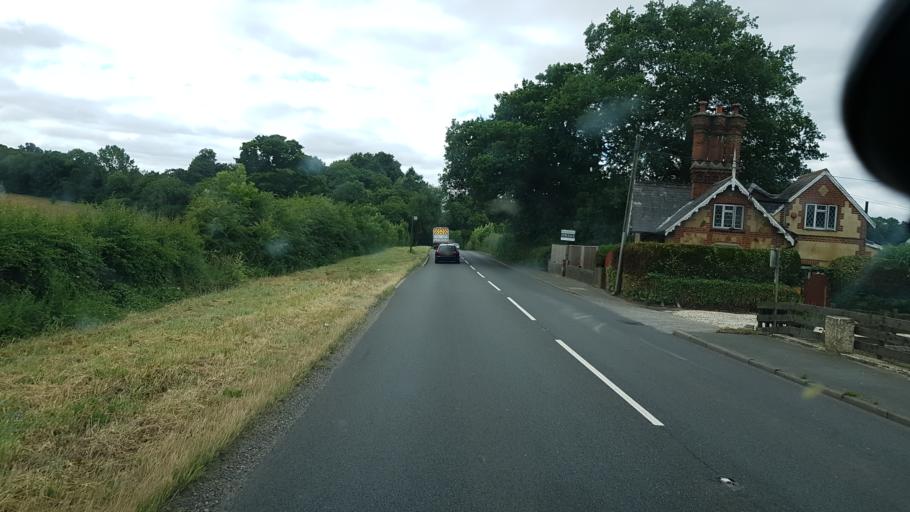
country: GB
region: England
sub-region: Surrey
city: Godstone
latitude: 51.2136
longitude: -0.0523
